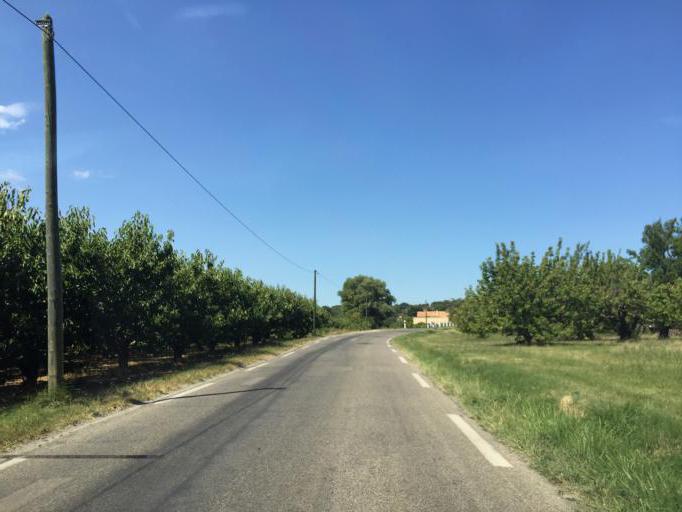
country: FR
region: Provence-Alpes-Cote d'Azur
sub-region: Departement du Vaucluse
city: Venasque
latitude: 44.0053
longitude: 5.1436
